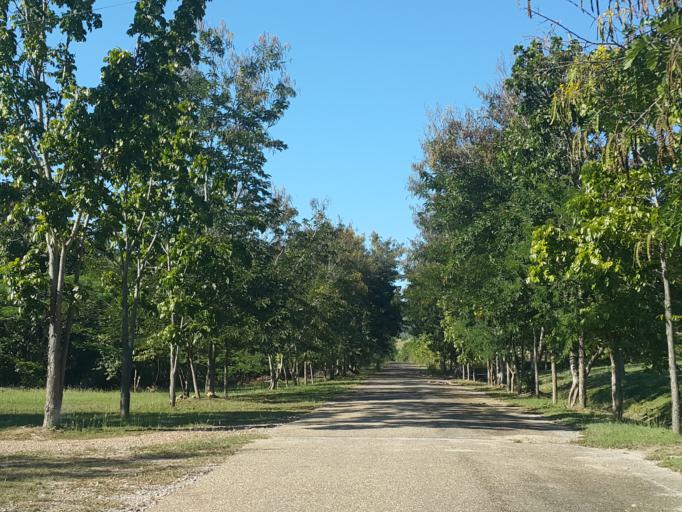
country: TH
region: Chiang Mai
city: San Sai
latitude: 18.9189
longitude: 99.1162
